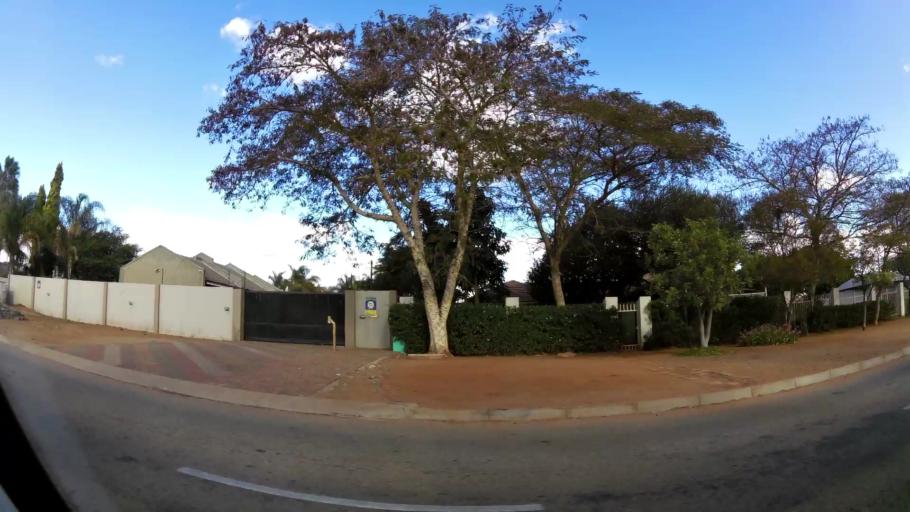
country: ZA
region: Limpopo
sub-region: Capricorn District Municipality
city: Polokwane
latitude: -23.9058
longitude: 29.4958
